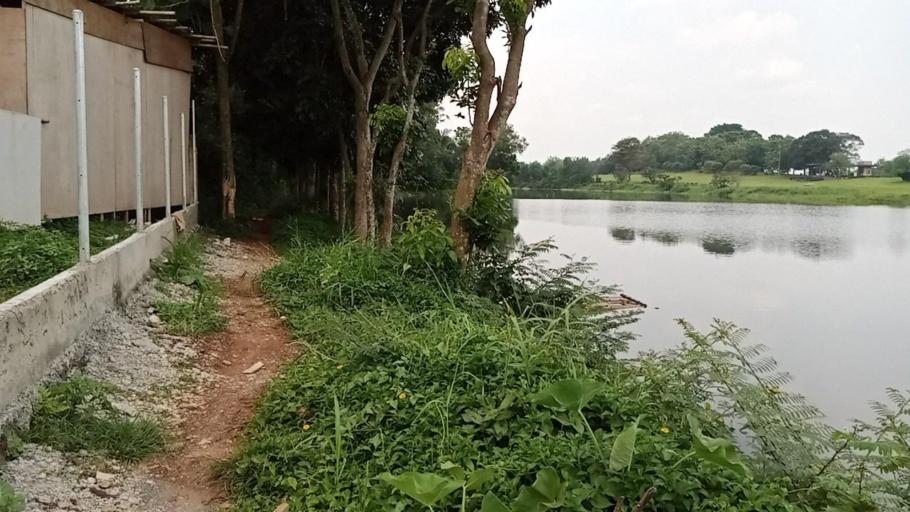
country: ID
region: West Java
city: Sawangan
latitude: -6.3887
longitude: 106.7554
